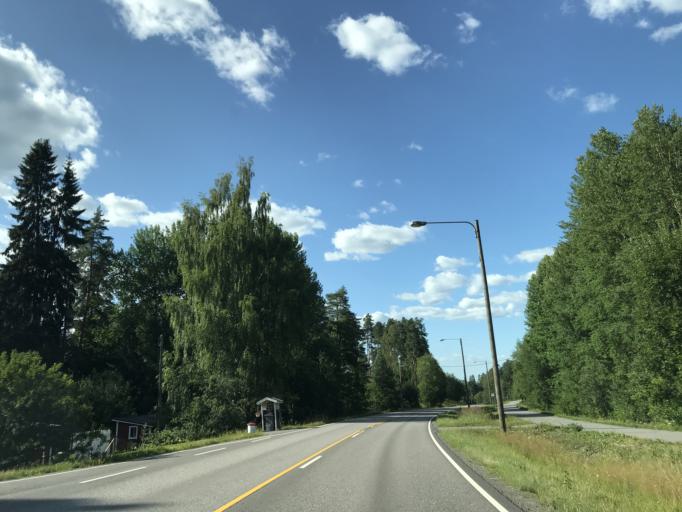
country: FI
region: Uusimaa
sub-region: Helsinki
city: Nurmijaervi
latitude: 60.4243
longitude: 24.8608
